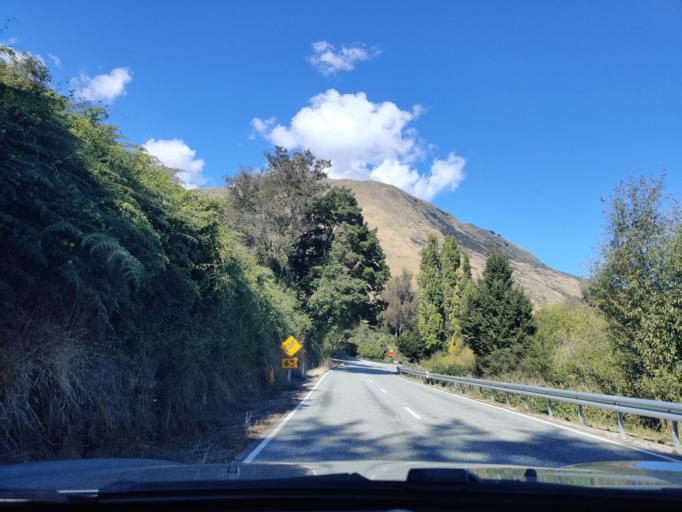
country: NZ
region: Otago
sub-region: Queenstown-Lakes District
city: Queenstown
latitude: -44.9991
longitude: 168.4376
